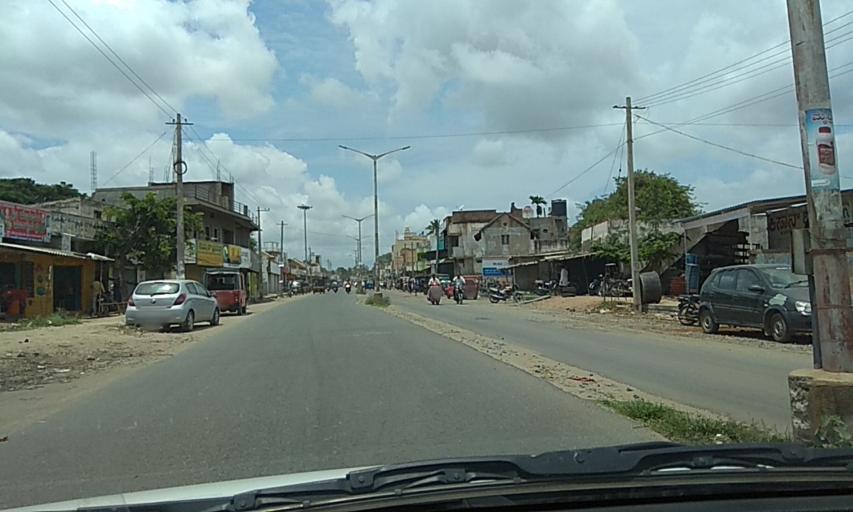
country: IN
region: Karnataka
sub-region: Chamrajnagar
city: Gundlupet
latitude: 11.8086
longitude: 76.6948
